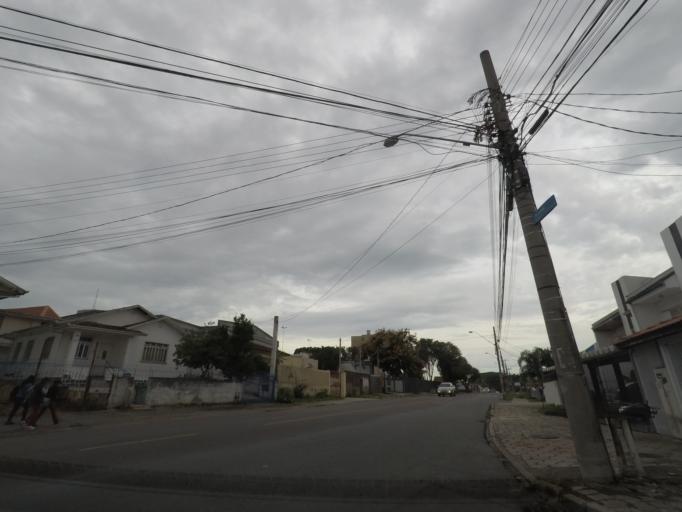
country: BR
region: Parana
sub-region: Curitiba
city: Curitiba
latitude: -25.4731
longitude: -49.3029
